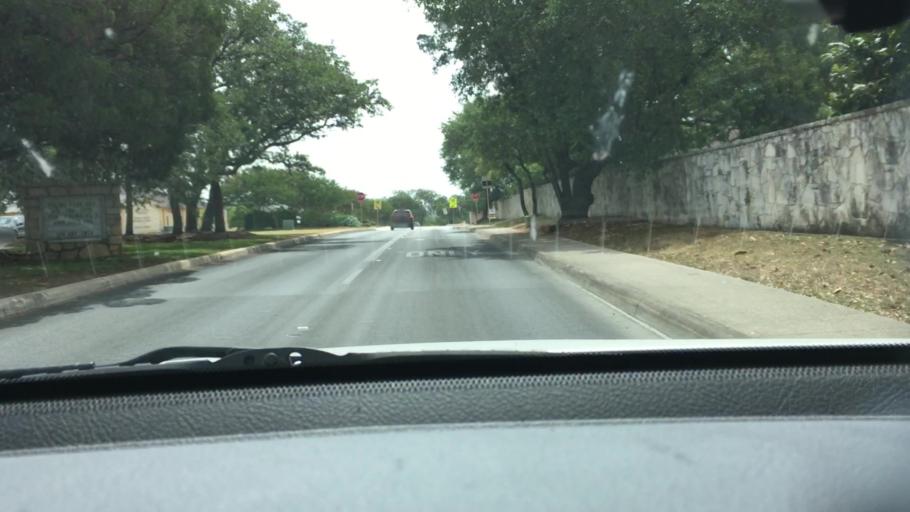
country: US
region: Texas
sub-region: Bexar County
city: Hollywood Park
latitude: 29.6300
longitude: -98.4553
